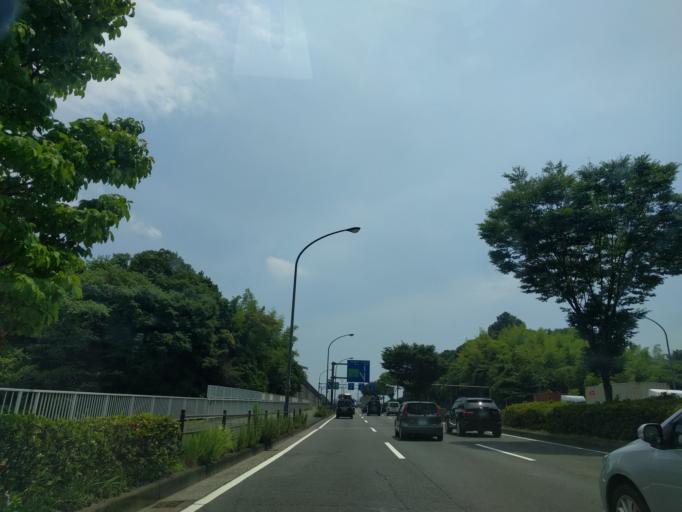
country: JP
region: Kanagawa
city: Yokohama
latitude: 35.4468
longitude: 139.5603
